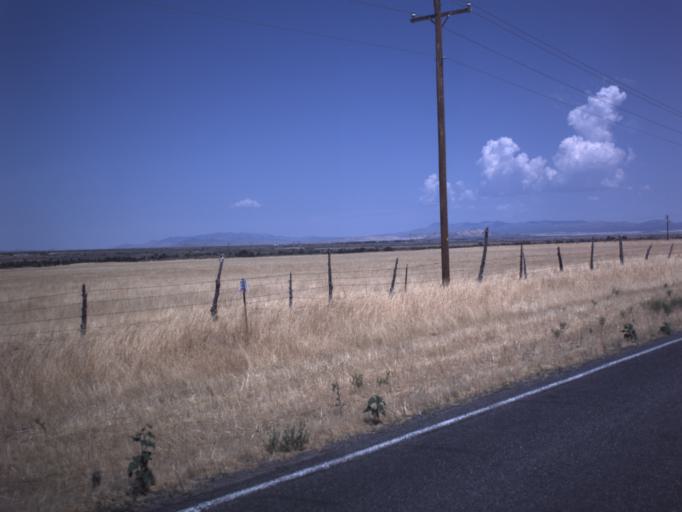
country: US
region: Utah
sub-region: Millard County
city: Delta
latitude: 39.4245
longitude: -112.3269
